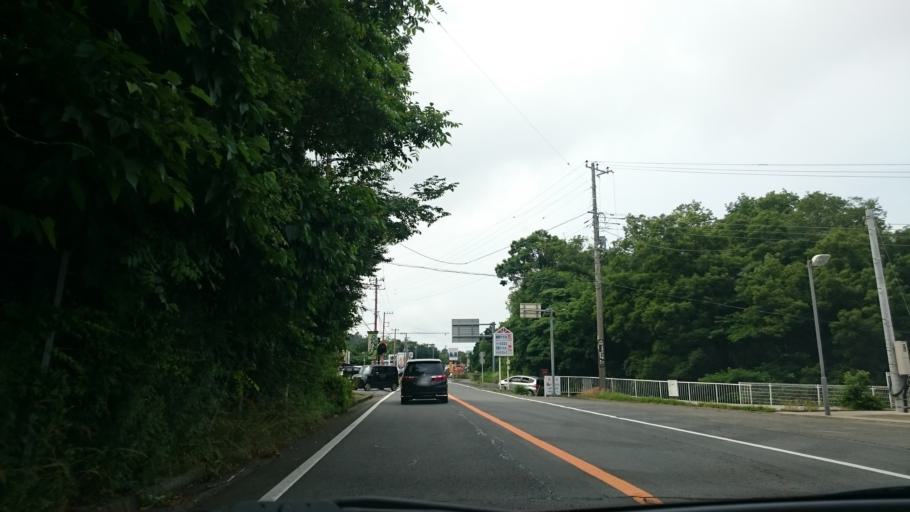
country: JP
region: Shizuoka
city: Ito
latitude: 34.9097
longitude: 139.1205
